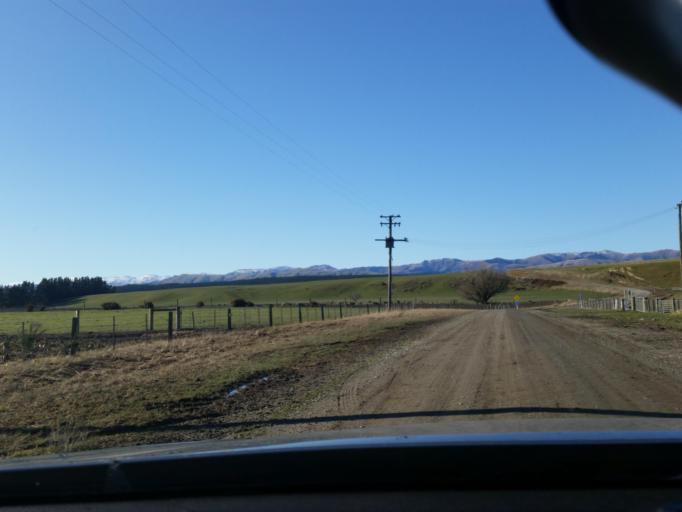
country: NZ
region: Otago
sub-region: Queenstown-Lakes District
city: Kingston
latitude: -45.7266
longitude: 168.7788
